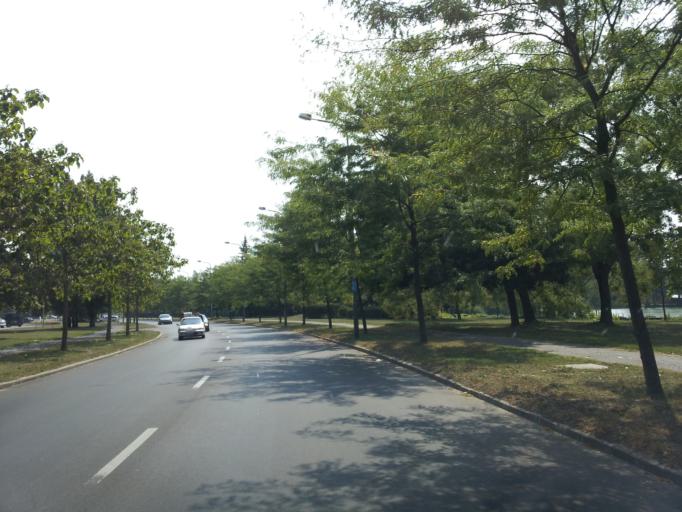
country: HU
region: Vas
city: Szombathely
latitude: 47.2337
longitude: 16.6029
